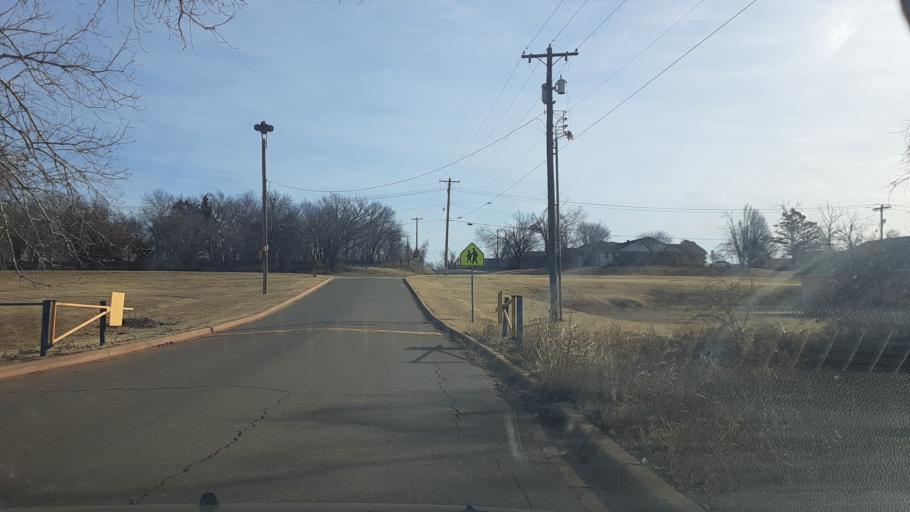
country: US
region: Oklahoma
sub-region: Logan County
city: Guthrie
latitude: 35.8926
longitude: -97.4174
